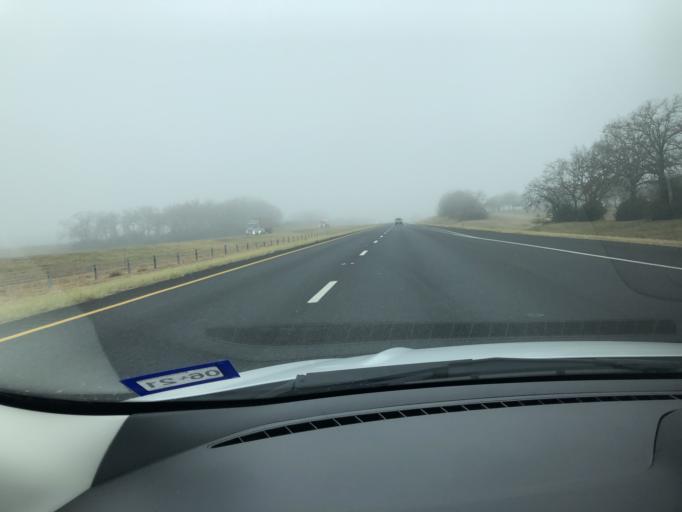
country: US
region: Texas
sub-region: Gonzales County
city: Waelder
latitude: 29.6579
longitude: -97.4211
